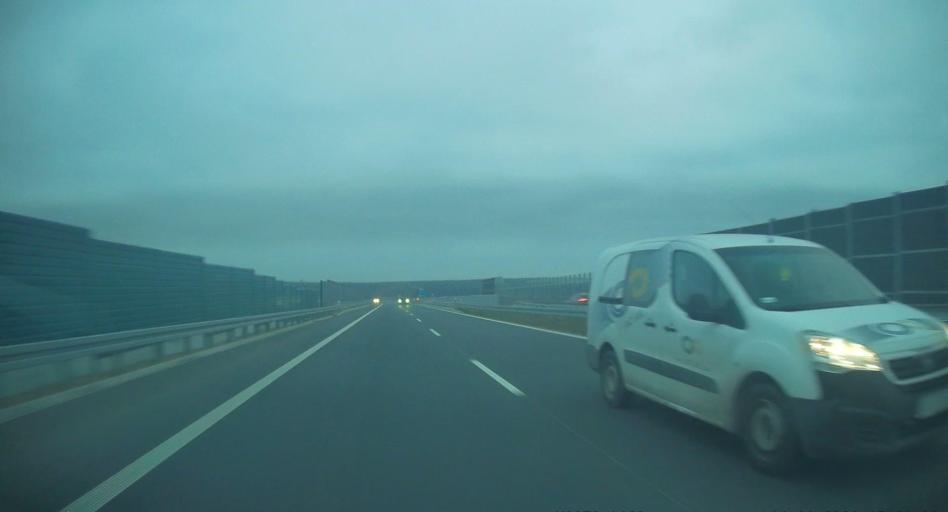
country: PL
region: Silesian Voivodeship
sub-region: Powiat bedzinski
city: Mierzecice
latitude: 50.4463
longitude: 19.1383
